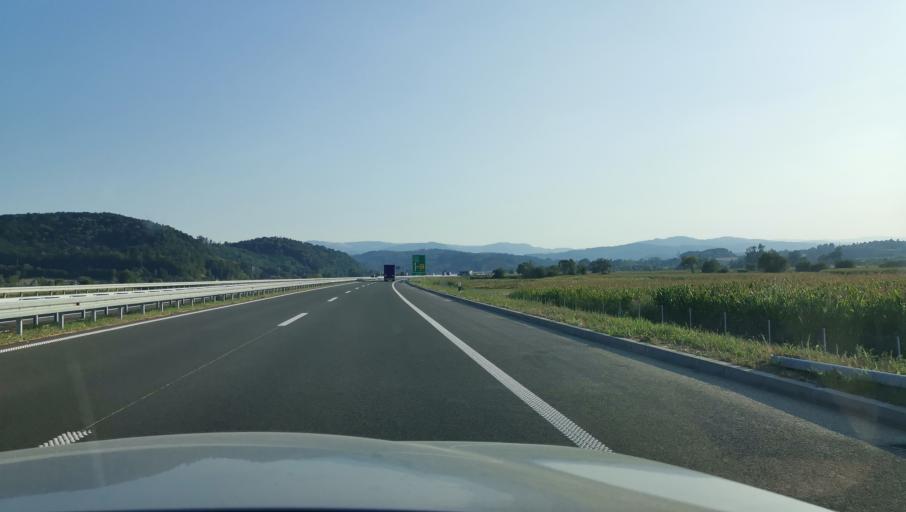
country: RS
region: Central Serbia
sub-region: Kolubarski Okrug
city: Ljig
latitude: 44.2484
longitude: 20.2677
